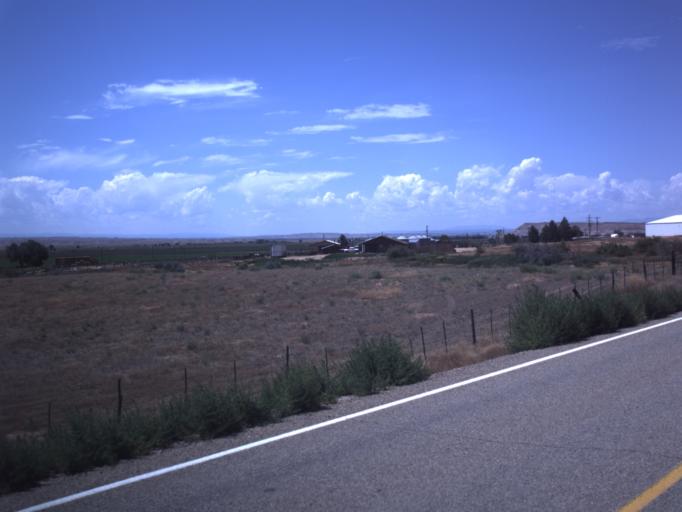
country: US
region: Utah
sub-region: Uintah County
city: Maeser
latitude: 40.2171
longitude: -109.6786
